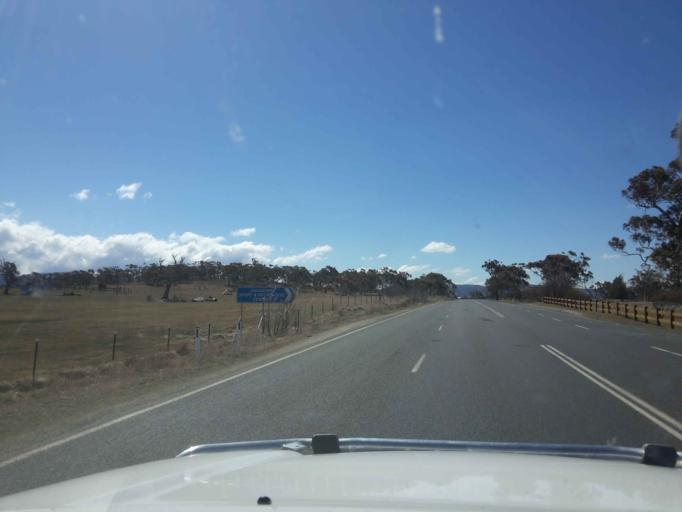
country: AU
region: New South Wales
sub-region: Snowy River
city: Jindabyne
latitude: -36.4324
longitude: 148.6088
